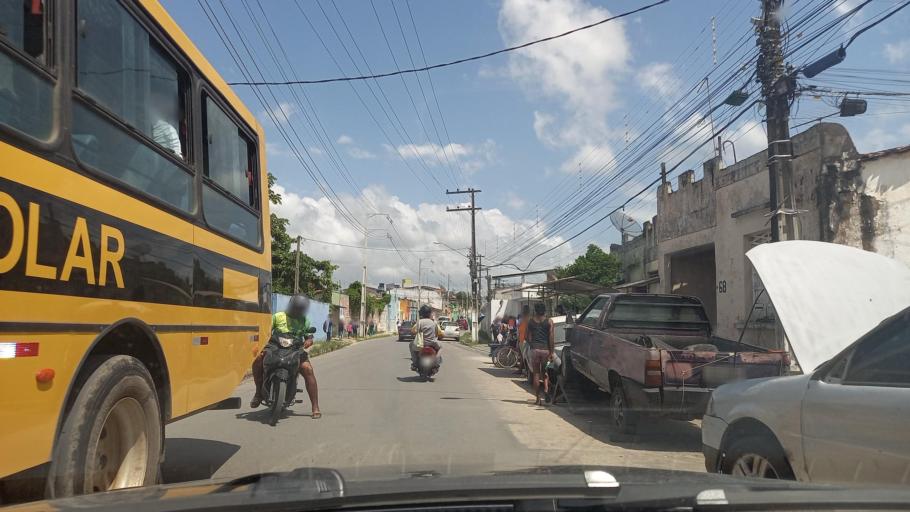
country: BR
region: Pernambuco
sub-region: Goiana
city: Goiana
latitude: -7.5637
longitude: -35.0007
